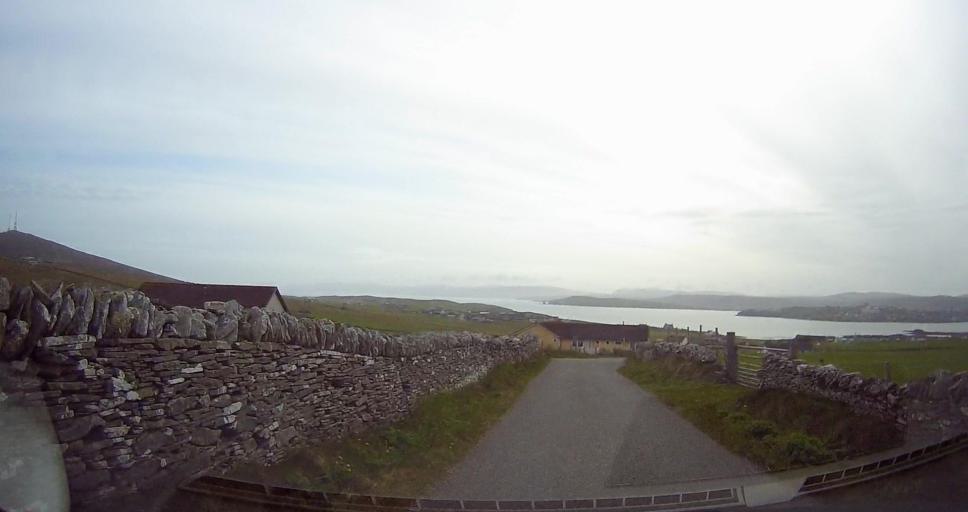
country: GB
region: Scotland
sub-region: Shetland Islands
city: Shetland
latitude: 60.1517
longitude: -1.0979
